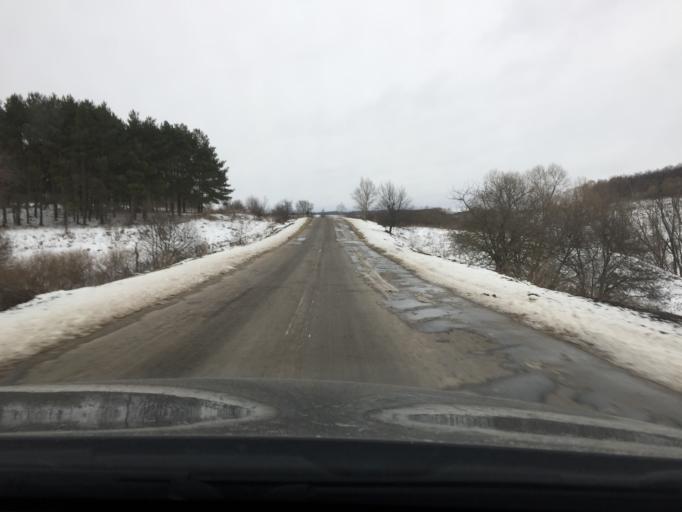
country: RU
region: Tula
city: Shchekino
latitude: 53.8290
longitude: 37.5600
